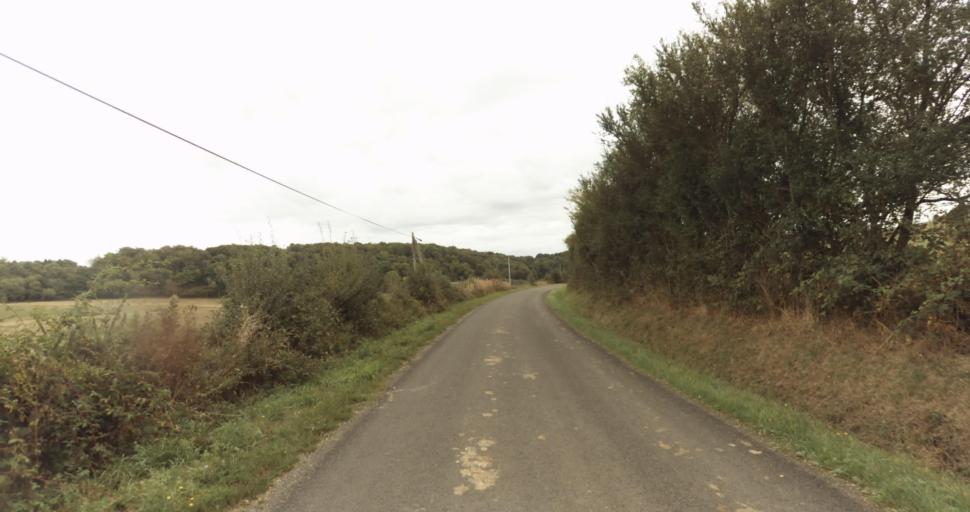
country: FR
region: Lower Normandy
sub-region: Departement de l'Orne
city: Vimoutiers
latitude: 48.9328
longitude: 0.3147
